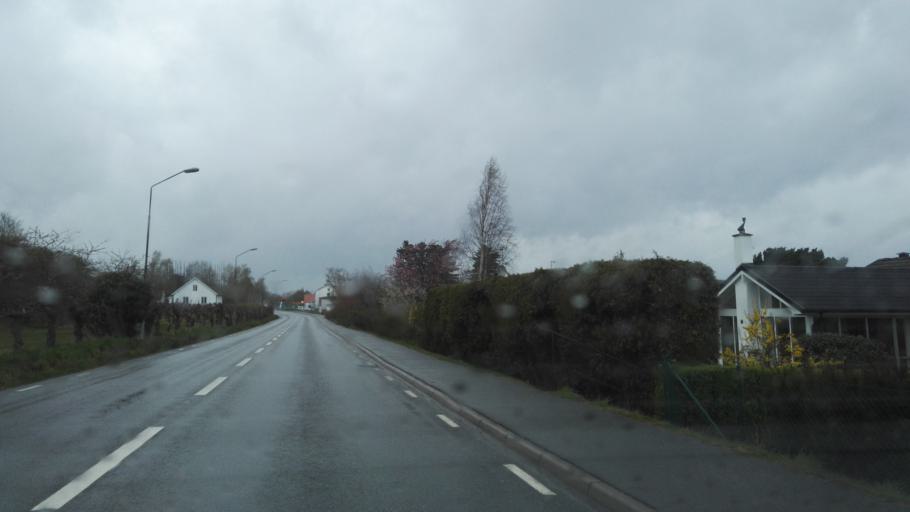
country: SE
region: Skane
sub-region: Simrishamns Kommun
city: Kivik
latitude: 55.6821
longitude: 14.2260
